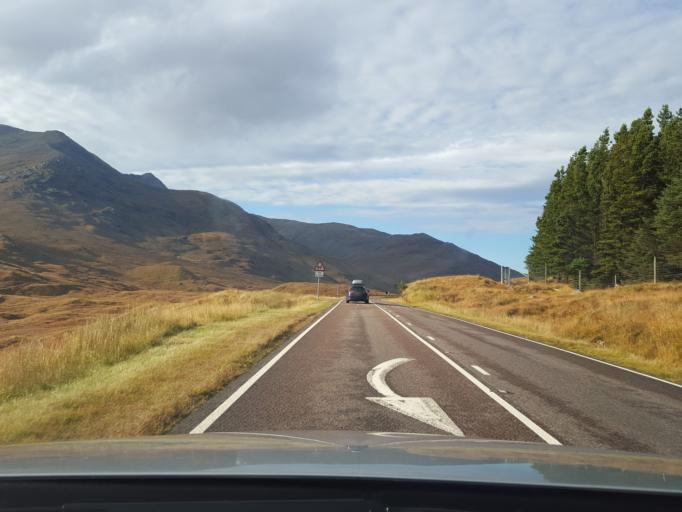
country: GB
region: Scotland
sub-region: Highland
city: Fort William
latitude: 57.1516
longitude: -5.2306
